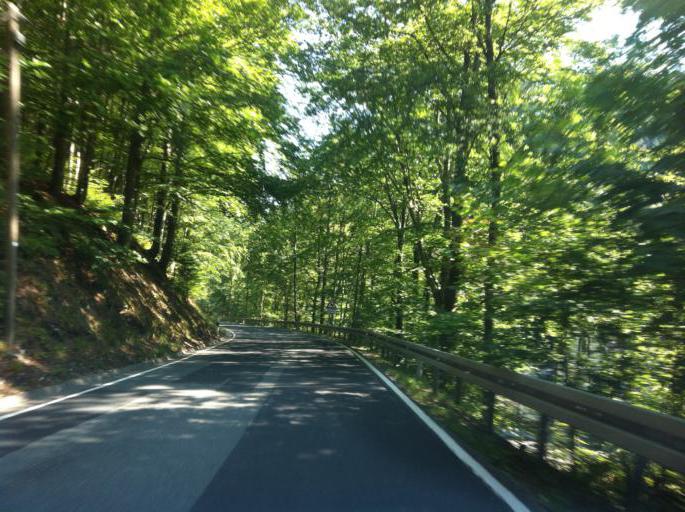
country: DE
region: Thuringia
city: Schalkau
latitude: 50.4289
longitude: 11.0419
